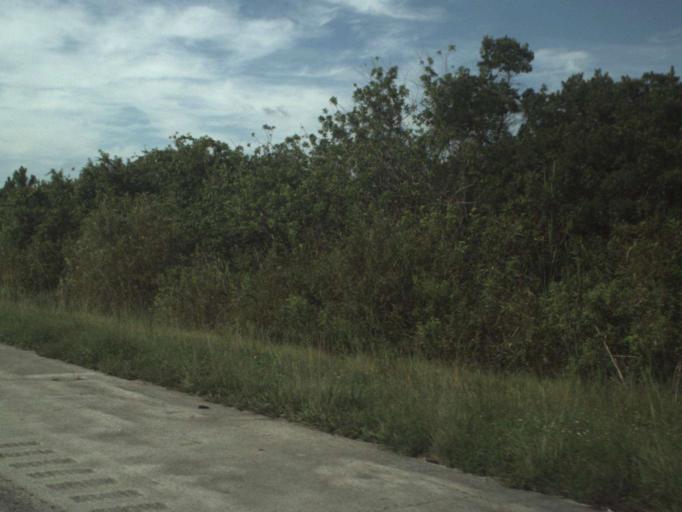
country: US
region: Florida
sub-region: Indian River County
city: Fellsmere
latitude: 27.7348
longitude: -80.5482
